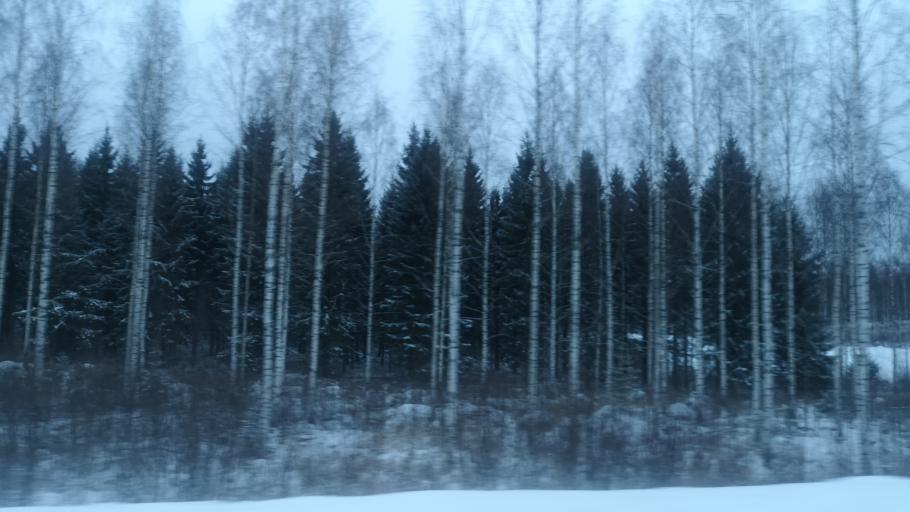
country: FI
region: Southern Savonia
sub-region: Savonlinna
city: Enonkoski
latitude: 62.1059
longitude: 28.6359
